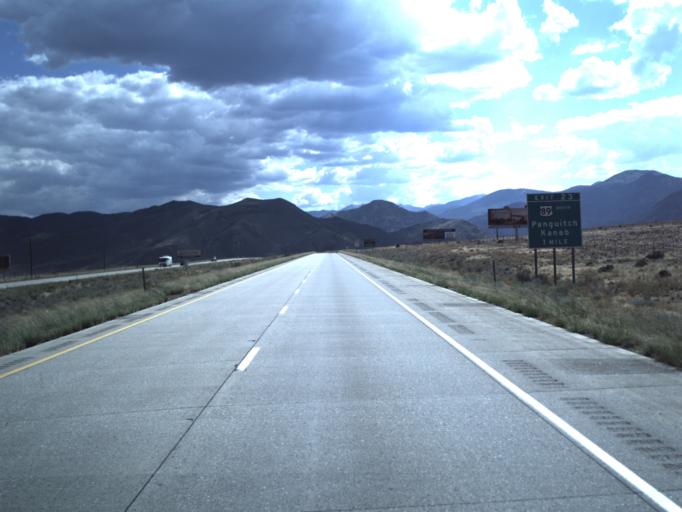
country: US
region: Utah
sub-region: Sevier County
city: Monroe
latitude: 38.6127
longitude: -112.2315
